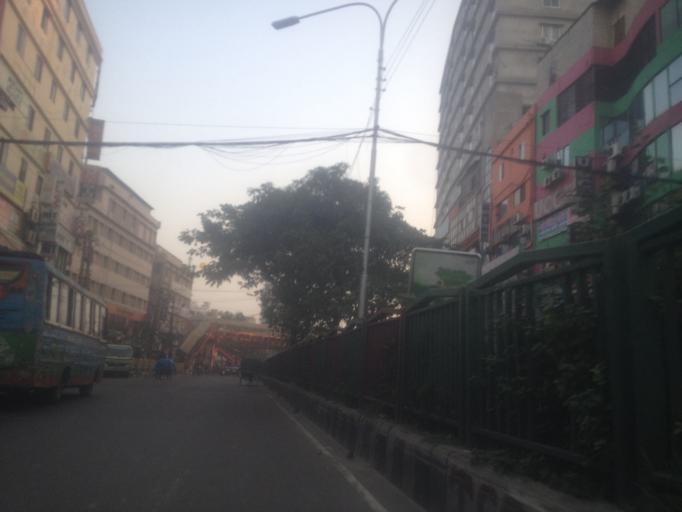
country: BD
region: Dhaka
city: Azimpur
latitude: 23.8058
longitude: 90.3690
